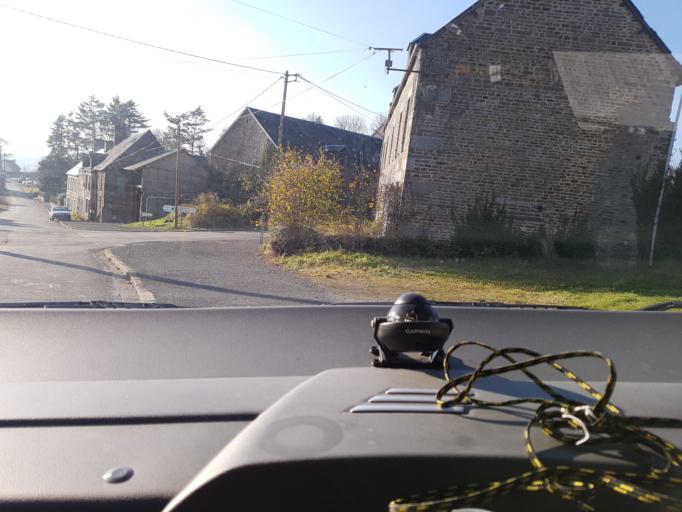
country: FR
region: Lower Normandy
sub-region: Departement du Calvados
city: Conde-sur-Noireau
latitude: 48.9187
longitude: -0.5765
